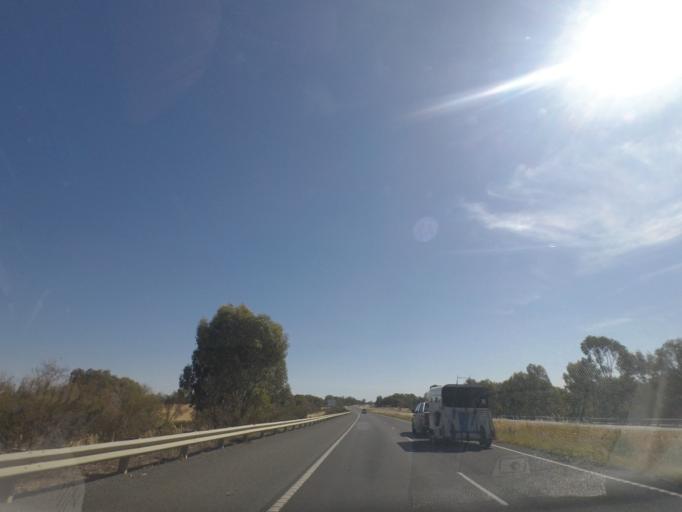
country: AU
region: Victoria
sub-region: Greater Shepparton
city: Shepparton
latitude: -36.6132
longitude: 145.3153
